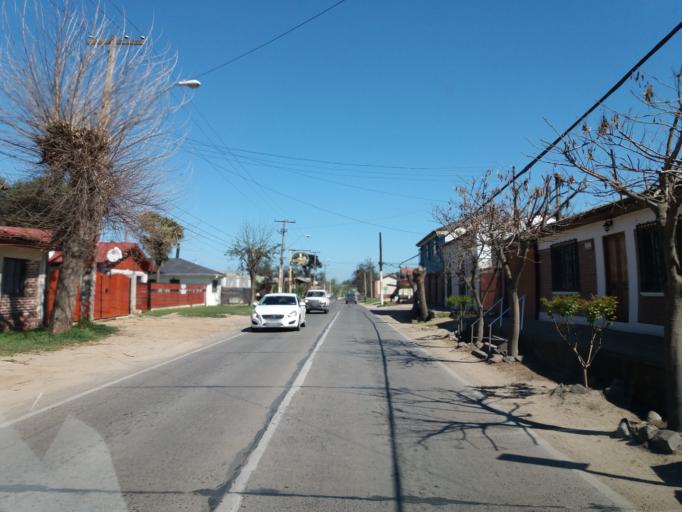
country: CL
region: Valparaiso
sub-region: Provincia de Marga Marga
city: Limache
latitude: -32.9964
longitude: -71.2261
